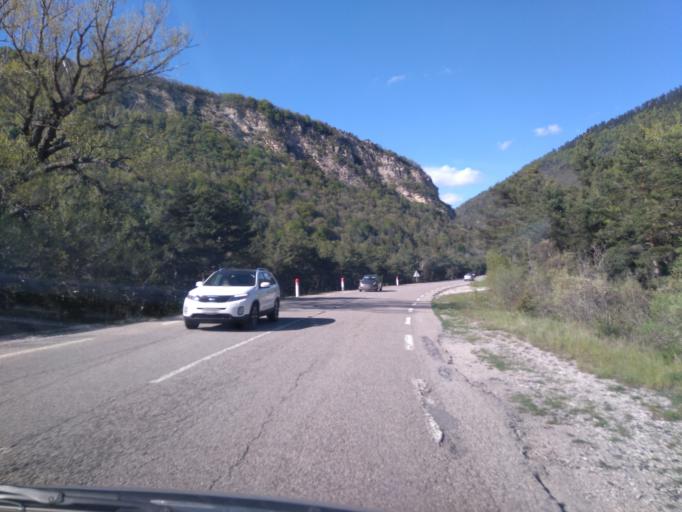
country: FR
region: Provence-Alpes-Cote d'Azur
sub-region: Departement des Hautes-Alpes
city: Veynes
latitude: 44.6395
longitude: 5.6959
